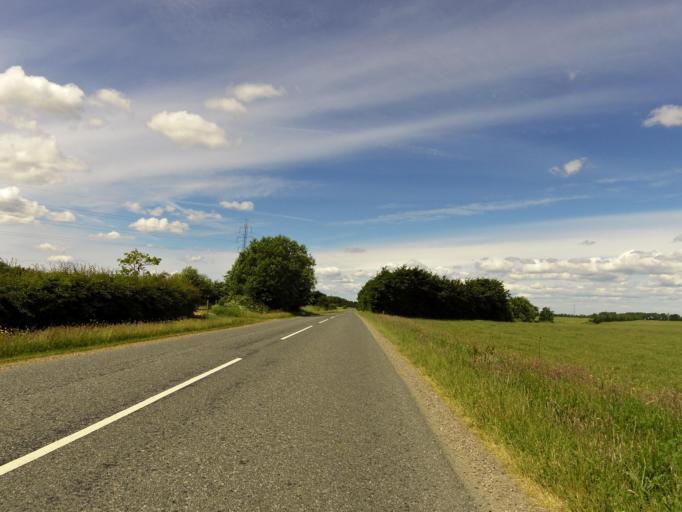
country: DK
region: South Denmark
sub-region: Esbjerg Kommune
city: Ribe
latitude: 55.2719
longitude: 8.8058
